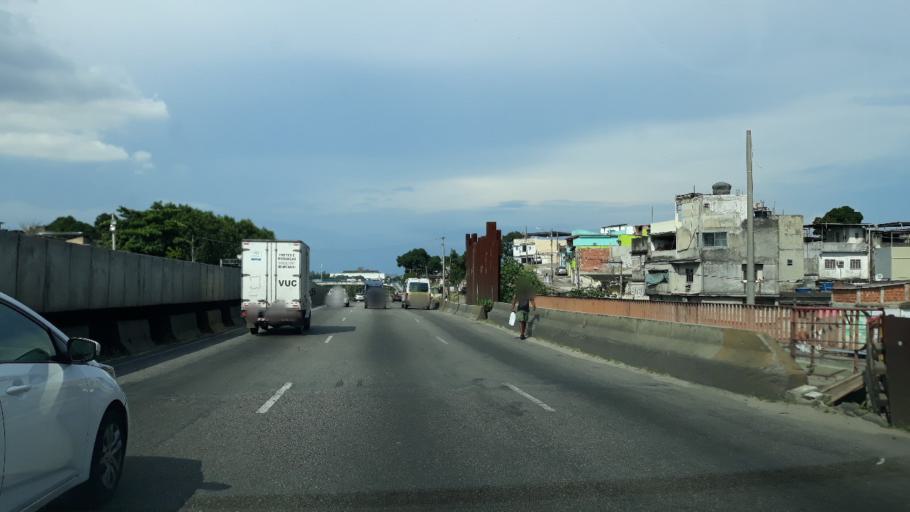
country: BR
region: Rio de Janeiro
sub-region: Sao Joao De Meriti
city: Sao Joao de Meriti
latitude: -22.8367
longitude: -43.3634
